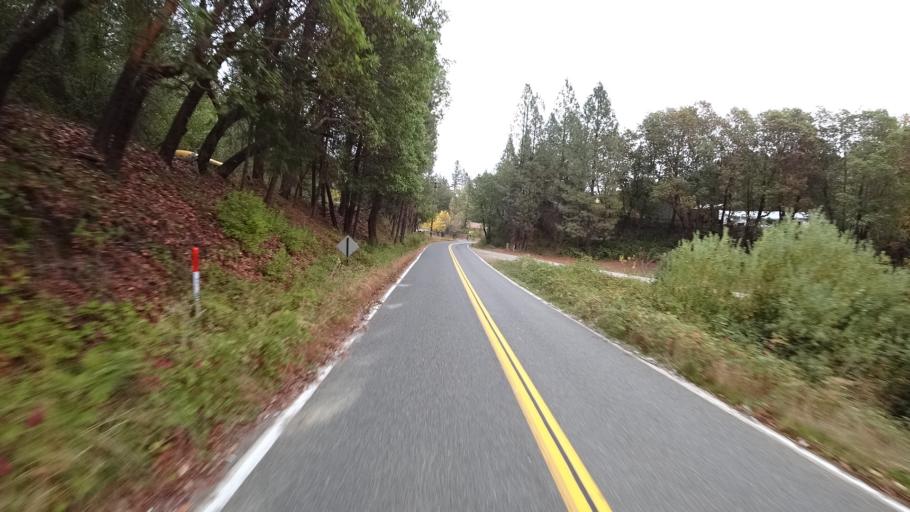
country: US
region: California
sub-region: Siskiyou County
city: Happy Camp
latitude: 41.7868
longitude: -123.3941
